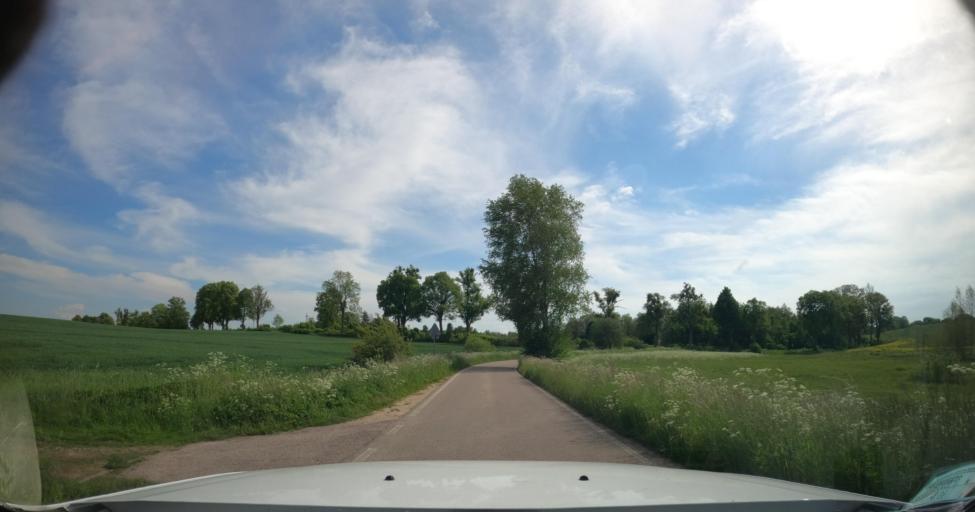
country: PL
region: Warmian-Masurian Voivodeship
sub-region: Powiat ostrodzki
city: Milakowo
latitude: 54.0136
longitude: 20.1522
